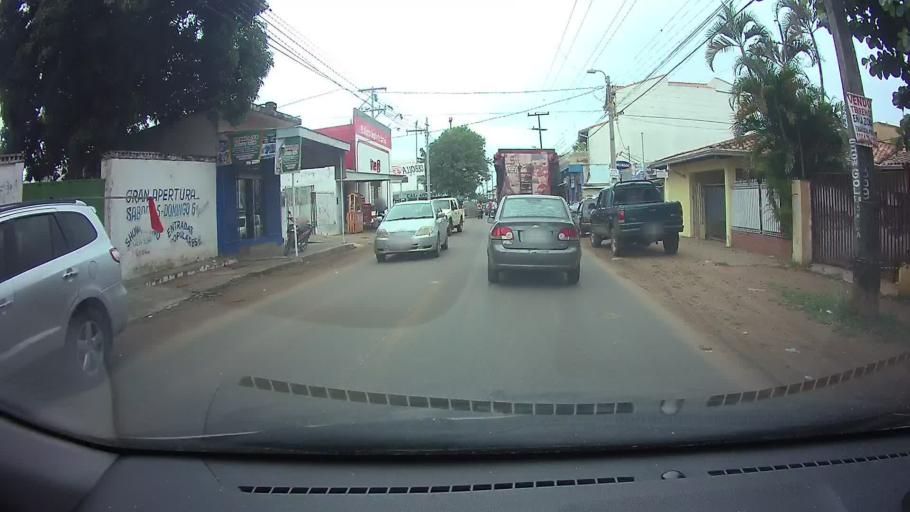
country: PY
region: Central
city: San Lorenzo
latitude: -25.3215
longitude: -57.4974
